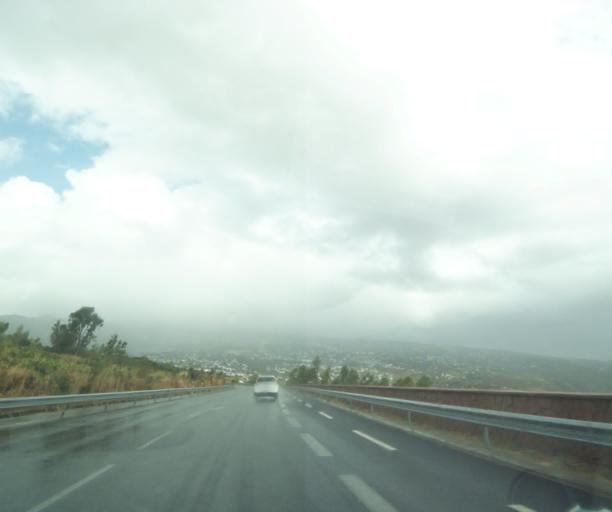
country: RE
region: Reunion
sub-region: Reunion
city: Le Port
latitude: -20.9715
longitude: 55.3135
